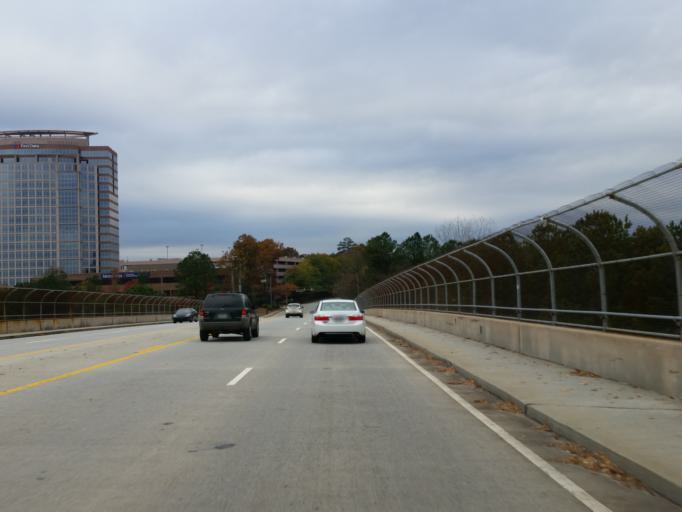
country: US
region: Georgia
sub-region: Fulton County
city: Sandy Springs
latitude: 33.9076
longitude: -84.3569
